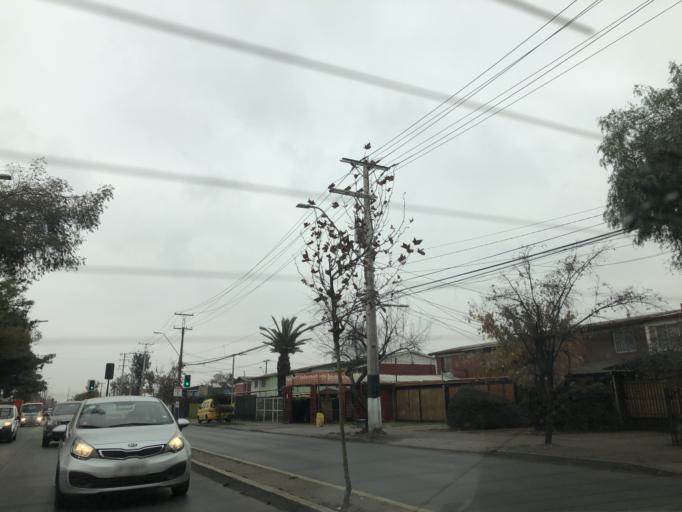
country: CL
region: Santiago Metropolitan
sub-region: Provincia de Santiago
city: La Pintana
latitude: -33.5817
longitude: -70.5998
